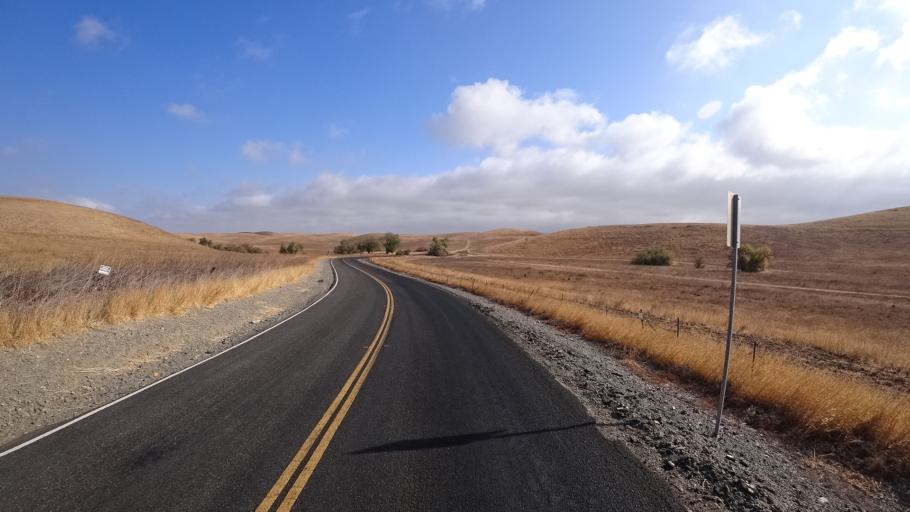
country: US
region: California
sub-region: Yolo County
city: Esparto
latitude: 38.7782
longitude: -121.9752
